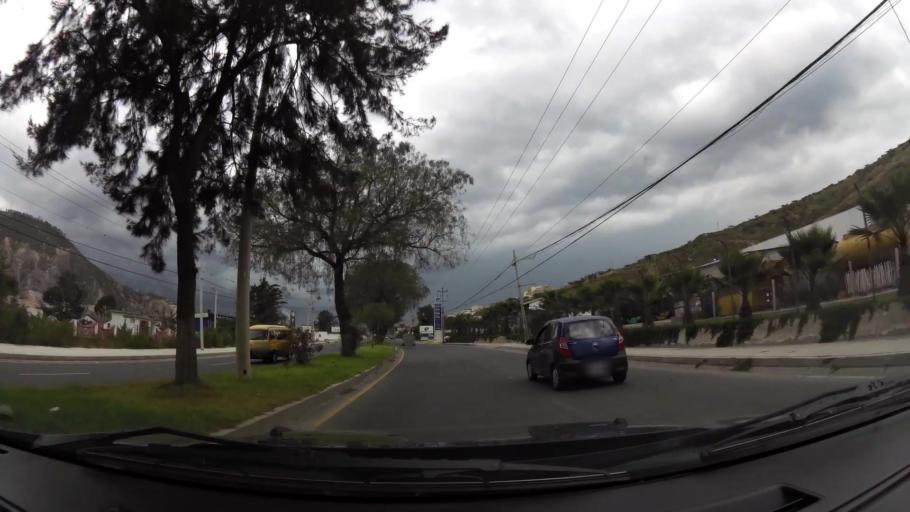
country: EC
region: Pichincha
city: Quito
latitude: -0.0417
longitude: -78.4555
